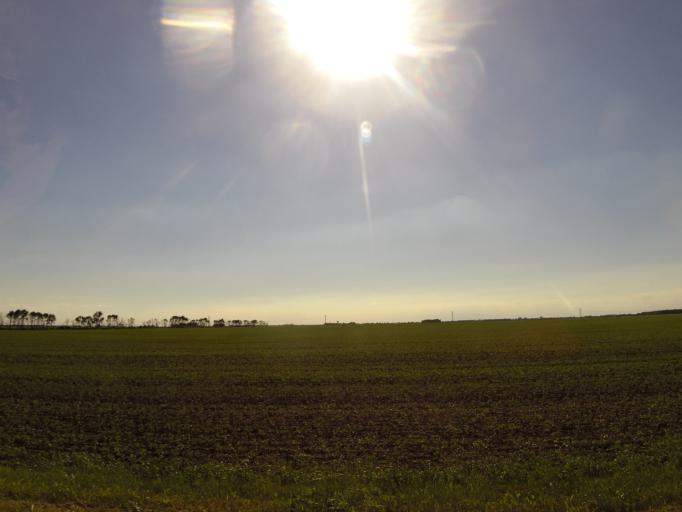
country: US
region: North Dakota
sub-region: Walsh County
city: Grafton
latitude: 48.4066
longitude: -97.2556
